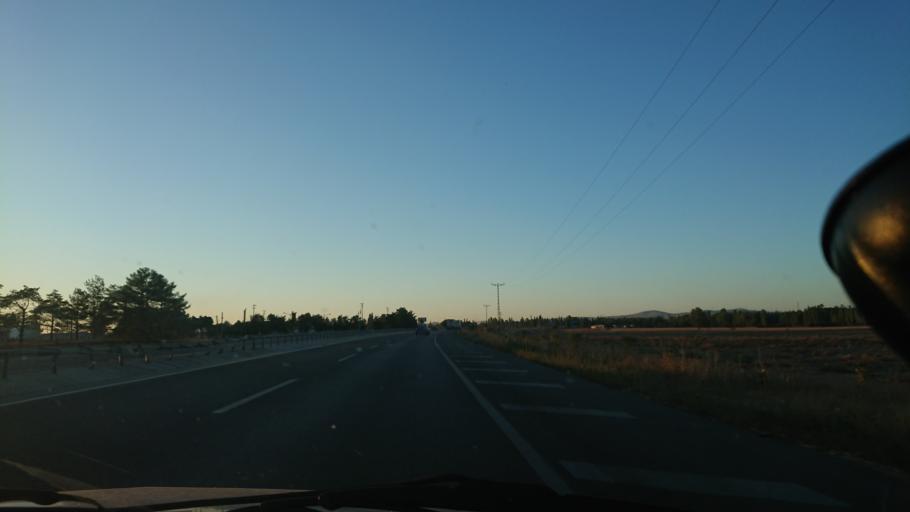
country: TR
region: Eskisehir
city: Mahmudiye
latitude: 39.5594
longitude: 30.9178
